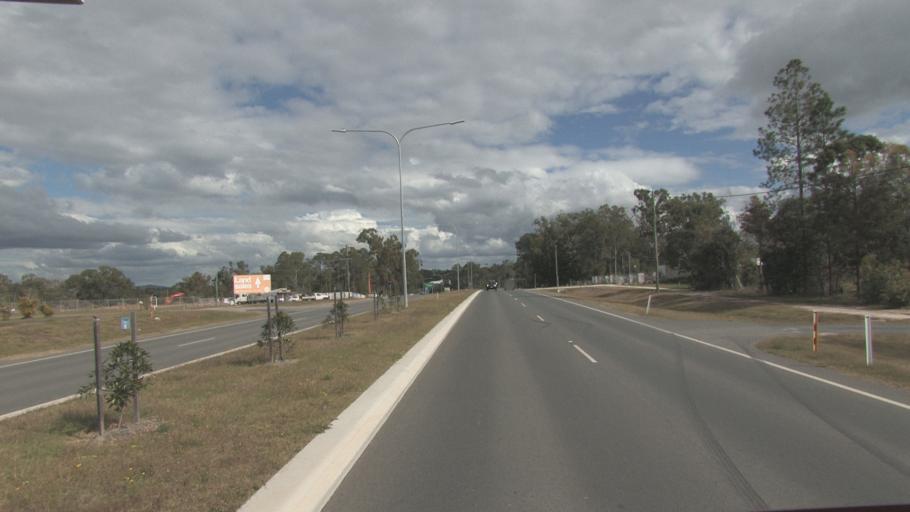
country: AU
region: Queensland
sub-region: Logan
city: Logan Reserve
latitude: -27.7046
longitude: 153.0957
